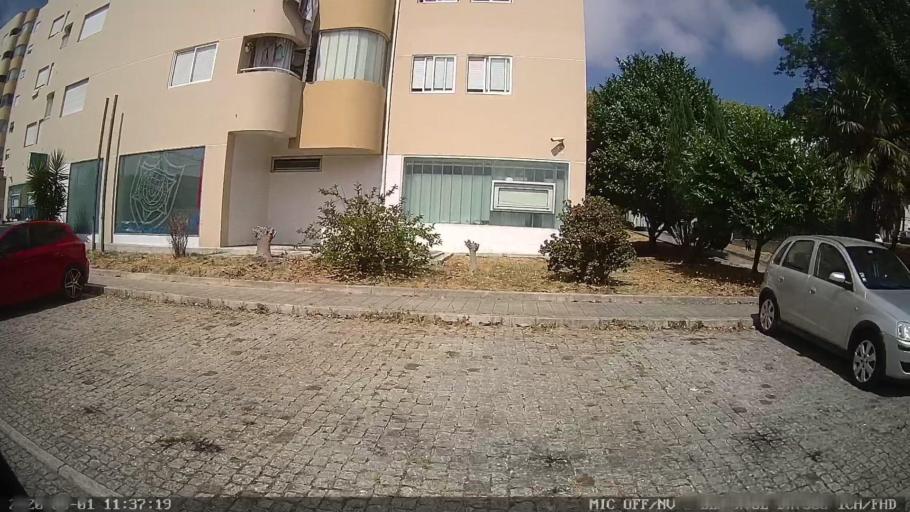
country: PT
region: Porto
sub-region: Matosinhos
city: Senhora da Hora
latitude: 41.1767
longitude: -8.6437
